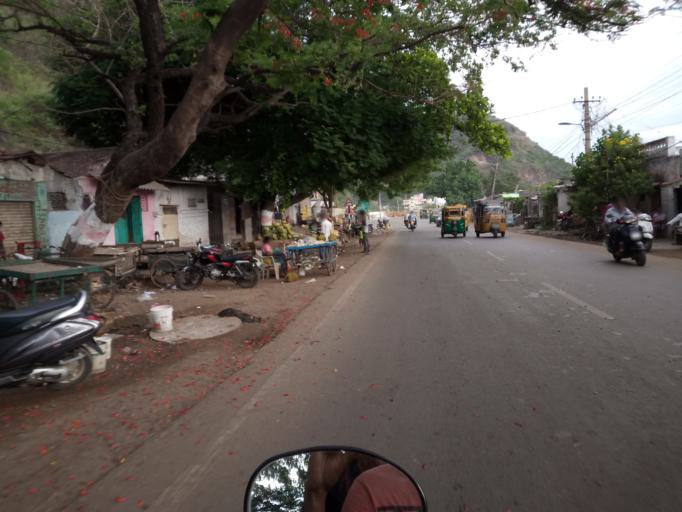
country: IN
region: Andhra Pradesh
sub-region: Guntur
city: Tadepalle
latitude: 16.4941
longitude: 80.6021
